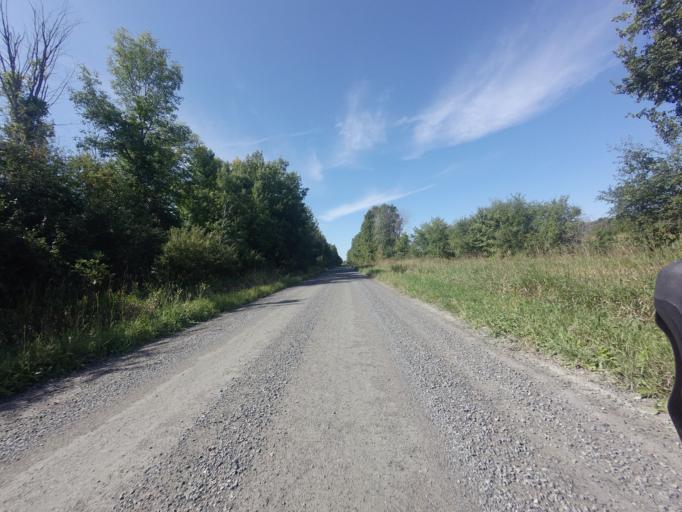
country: CA
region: Ontario
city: Perth
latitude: 44.9584
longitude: -76.3355
